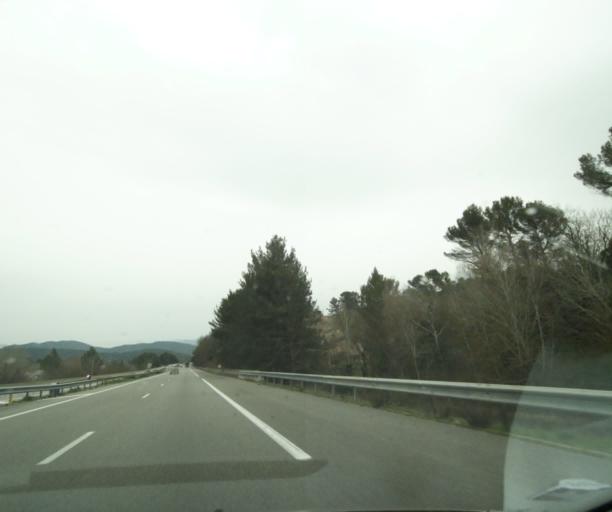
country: FR
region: Provence-Alpes-Cote d'Azur
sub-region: Departement des Bouches-du-Rhone
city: La Bouilladisse
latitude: 43.3935
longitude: 5.5851
